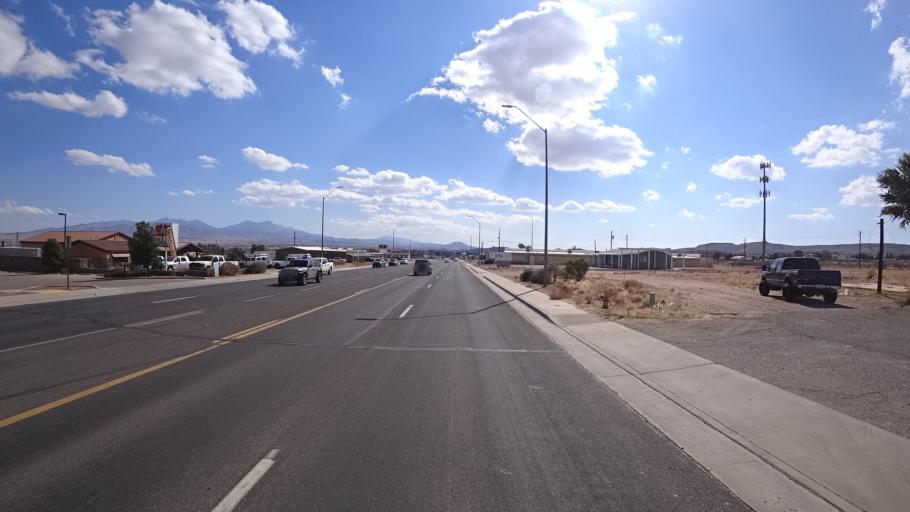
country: US
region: Arizona
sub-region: Mohave County
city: New Kingman-Butler
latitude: 35.2481
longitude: -114.0388
